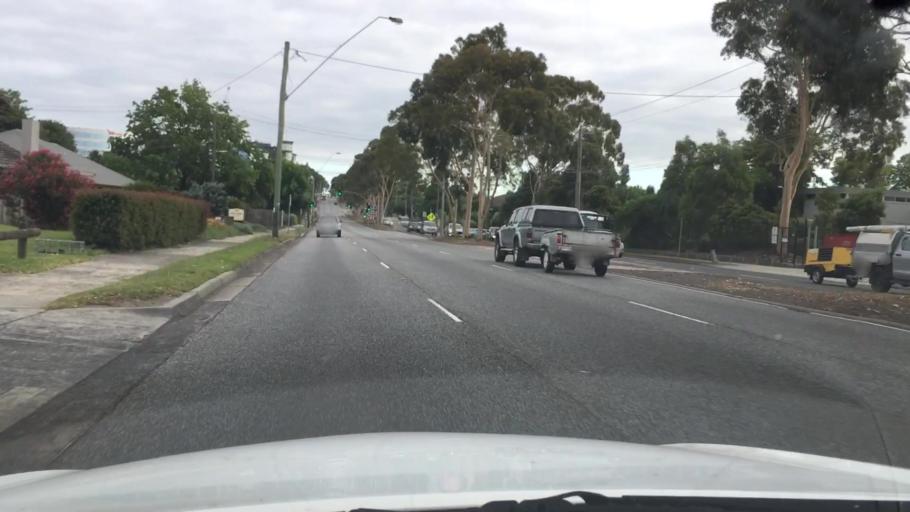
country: AU
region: Victoria
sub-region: Monash
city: Notting Hill
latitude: -37.8864
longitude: 145.1645
